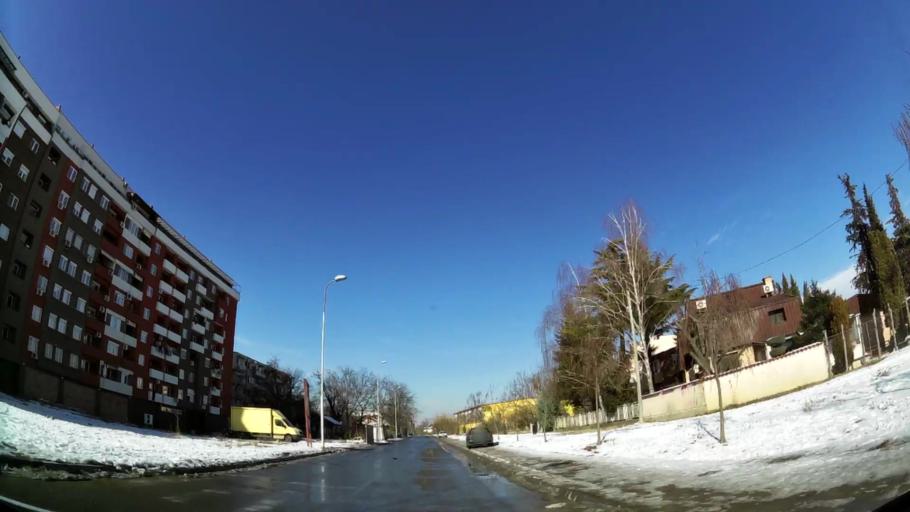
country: MK
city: Krushopek
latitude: 42.0027
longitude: 21.3633
